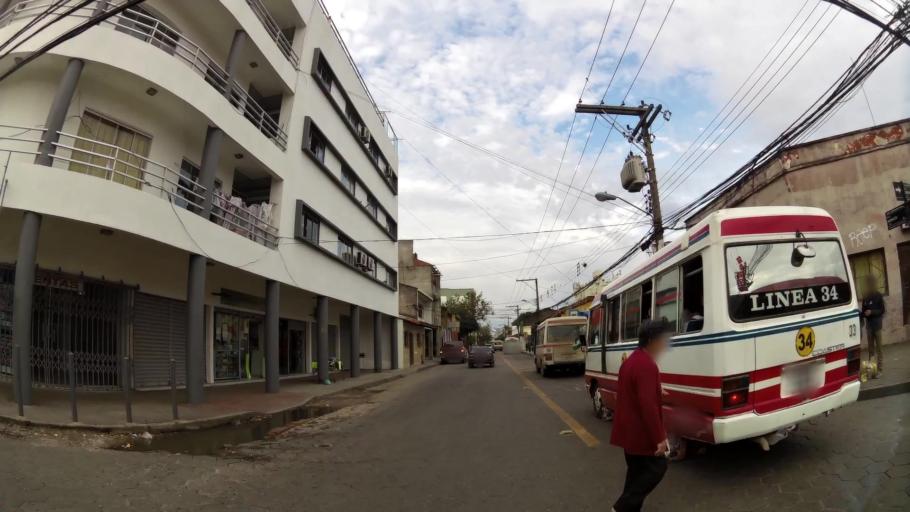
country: BO
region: Santa Cruz
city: Santa Cruz de la Sierra
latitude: -17.7813
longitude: -63.1765
